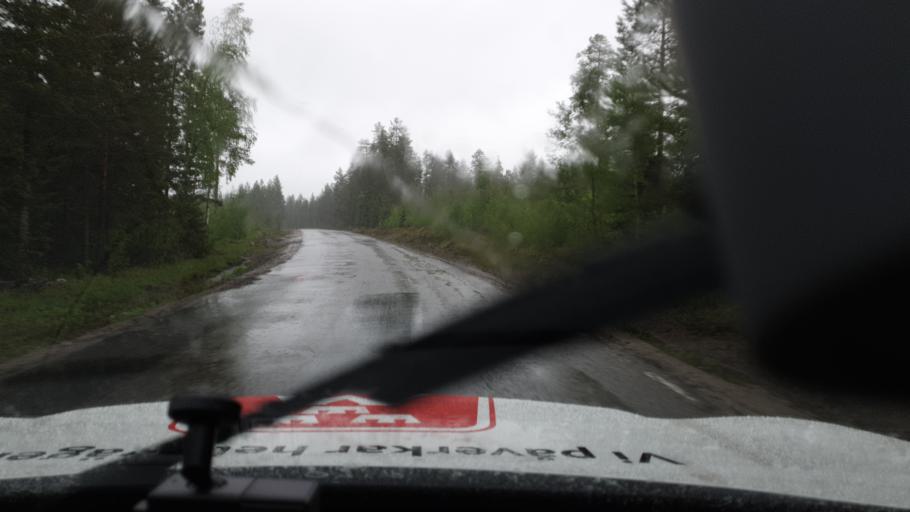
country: SE
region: Vaesterbotten
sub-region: Umea Kommun
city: Roback
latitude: 64.0183
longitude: 20.0821
